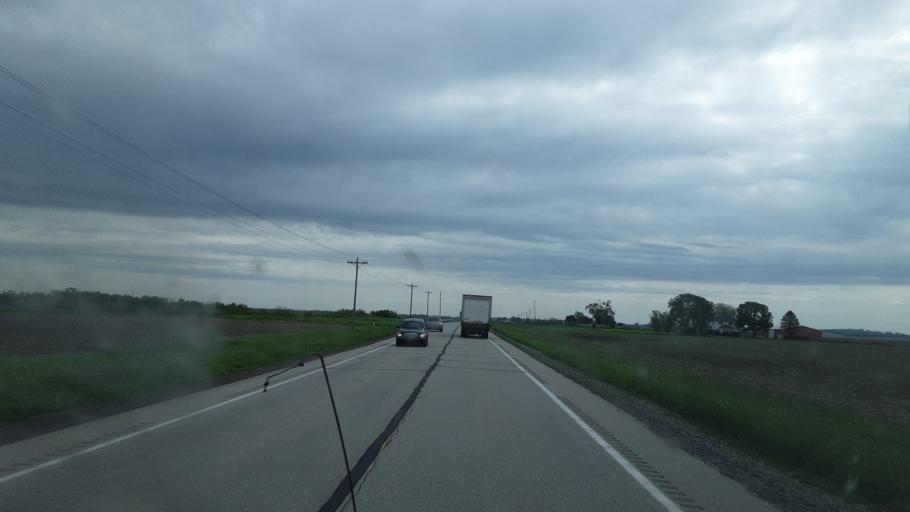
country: US
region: Illinois
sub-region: Mason County
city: Mason City
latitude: 40.3042
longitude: -89.7376
